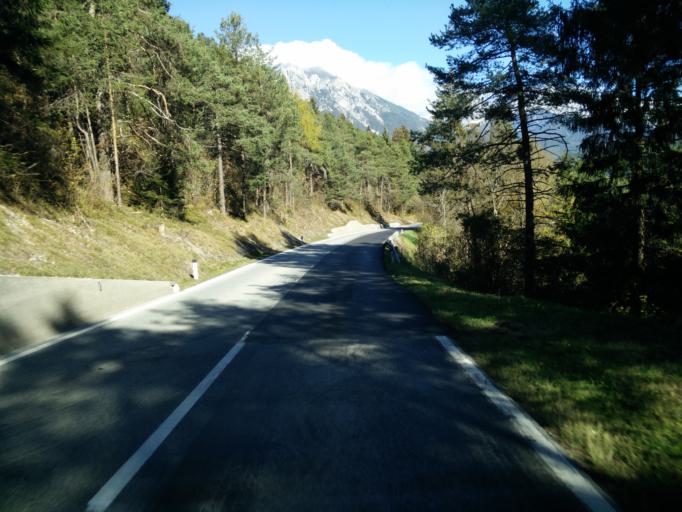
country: AT
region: Tyrol
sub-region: Politischer Bezirk Imst
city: Nassereith
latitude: 47.2913
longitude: 10.8249
